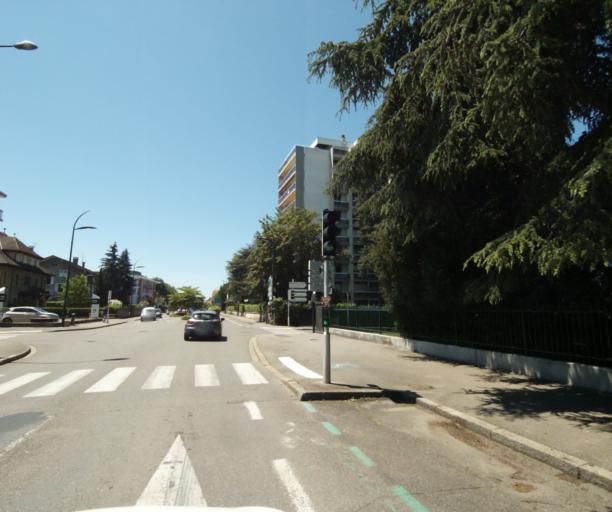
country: FR
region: Rhone-Alpes
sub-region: Departement de la Haute-Savoie
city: Thonon-les-Bains
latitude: 46.3688
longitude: 6.4737
